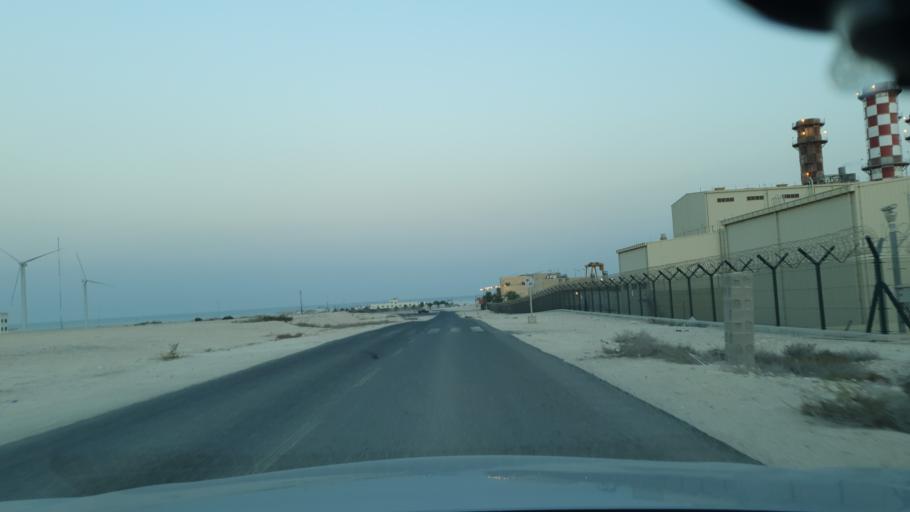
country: BH
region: Central Governorate
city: Dar Kulayb
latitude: 25.9733
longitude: 50.6062
